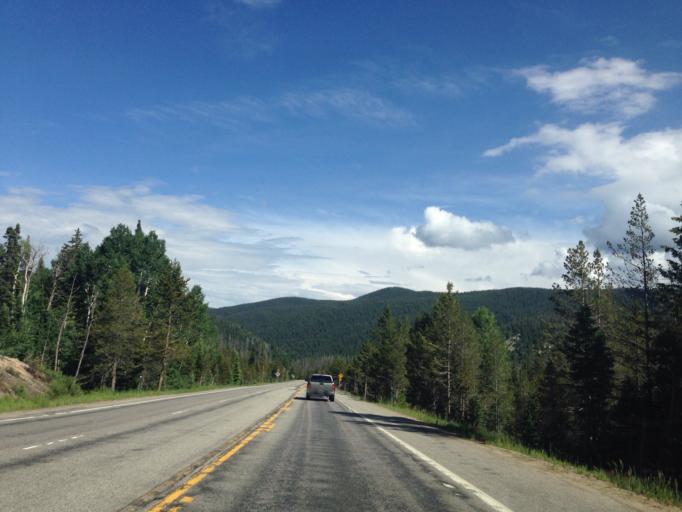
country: US
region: Colorado
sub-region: Routt County
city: Steamboat Springs
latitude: 40.3546
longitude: -106.7489
